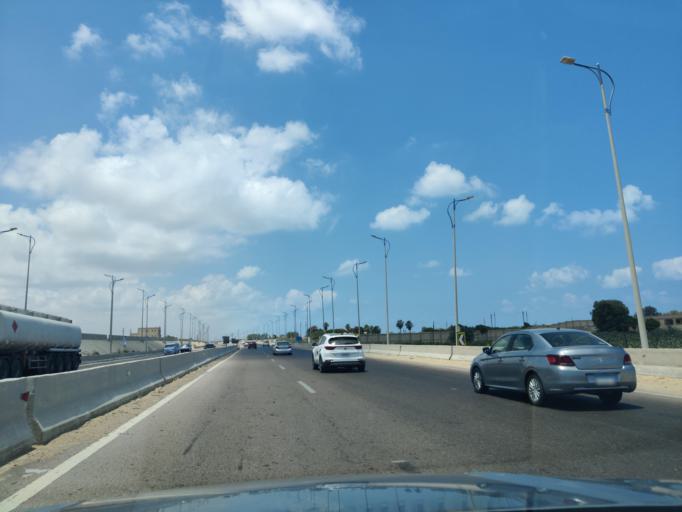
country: EG
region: Alexandria
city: Alexandria
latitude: 30.9470
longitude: 29.5135
